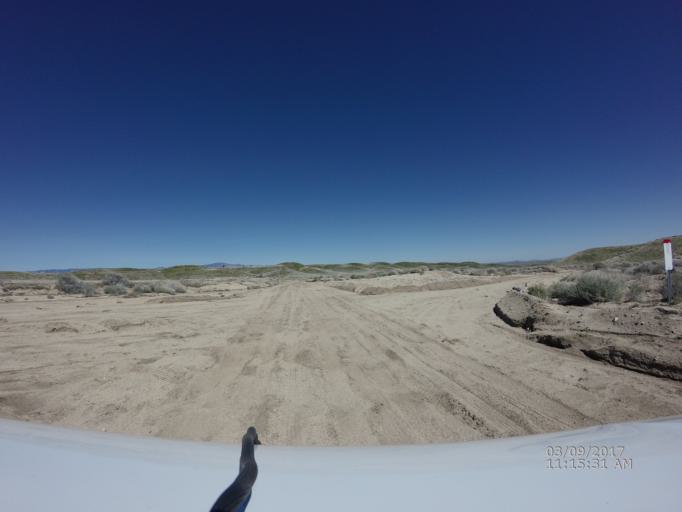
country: US
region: California
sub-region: Los Angeles County
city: Green Valley
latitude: 34.7057
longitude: -118.3949
